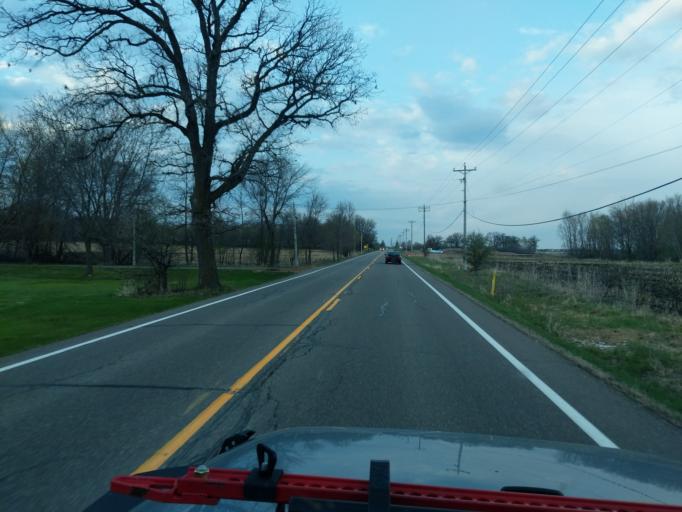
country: US
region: Minnesota
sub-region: Hennepin County
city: Rogers
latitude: 45.1483
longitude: -93.5220
